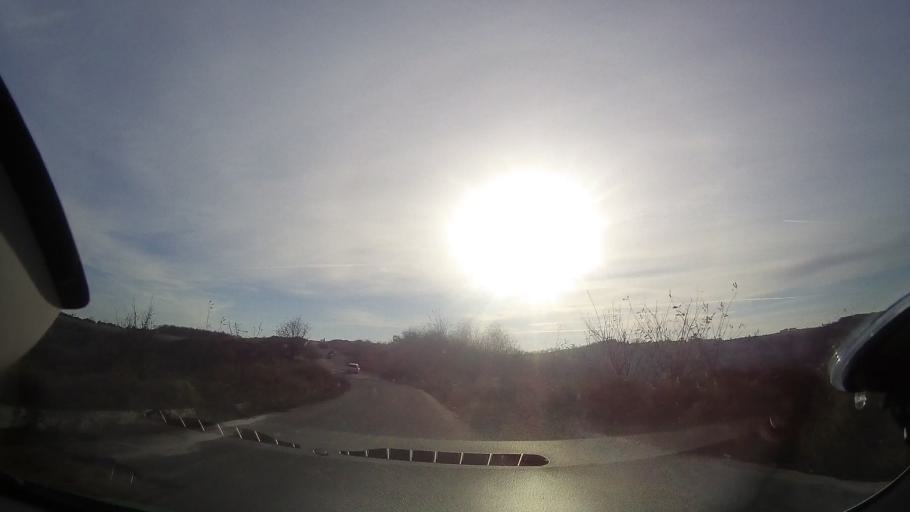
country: RO
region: Bihor
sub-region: Comuna Sarbi
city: Burzuc
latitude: 47.1301
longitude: 22.1869
